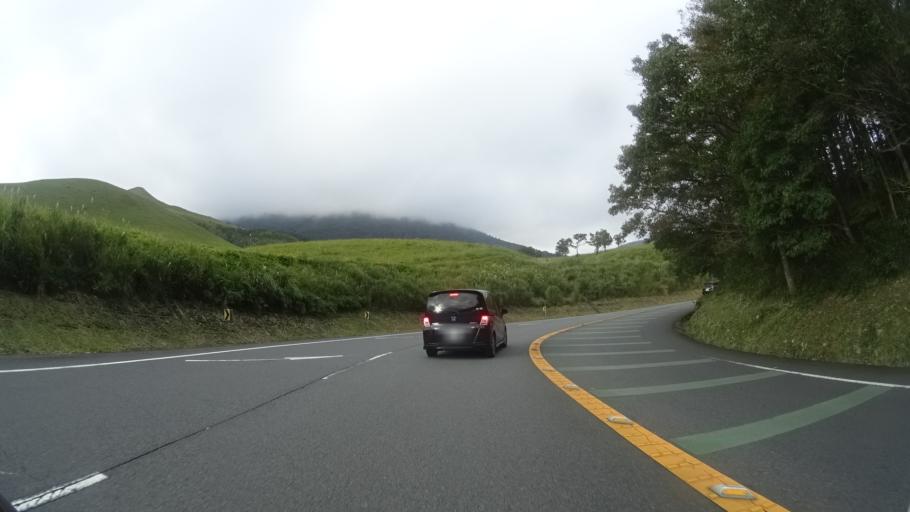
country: JP
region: Oita
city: Beppu
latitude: 33.2644
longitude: 131.3935
